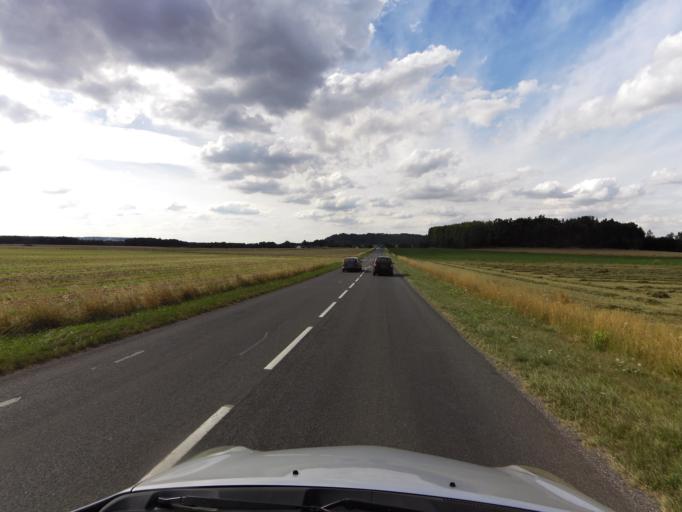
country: FR
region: Picardie
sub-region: Departement de l'Aisne
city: Bruyeres-et-Montberault
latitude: 49.5399
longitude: 3.6409
